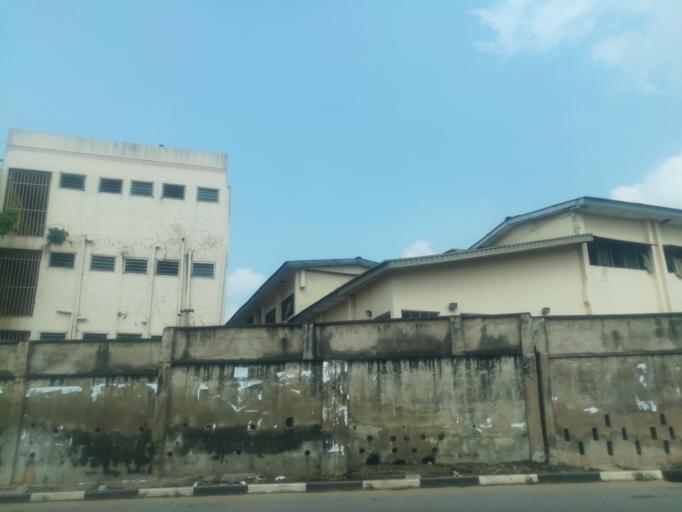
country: NG
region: Oyo
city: Ibadan
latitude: 7.3971
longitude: 3.9081
